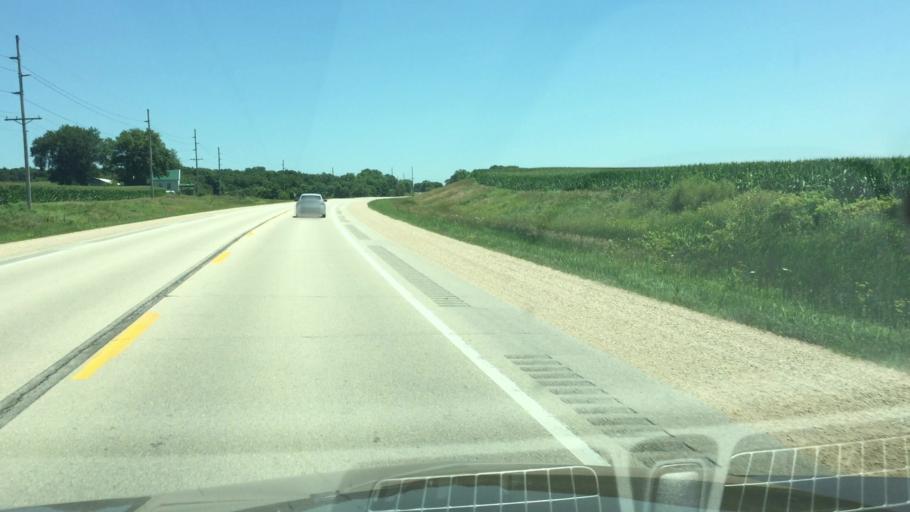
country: US
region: Iowa
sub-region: Jackson County
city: Maquoketa
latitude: 42.0645
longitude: -90.7654
